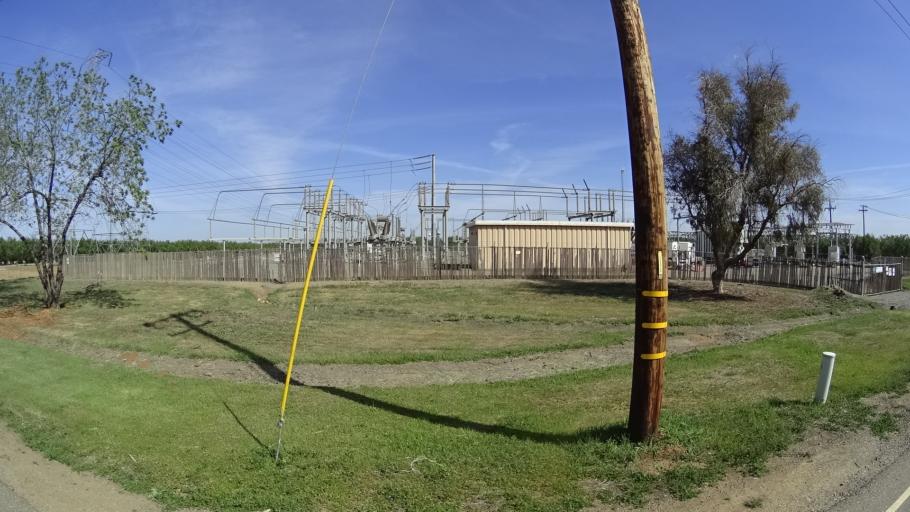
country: US
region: California
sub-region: Glenn County
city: Willows
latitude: 39.5388
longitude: -122.2631
